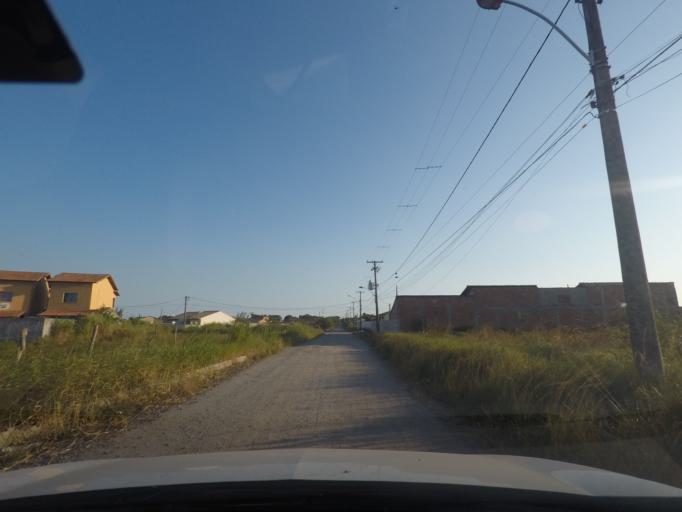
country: BR
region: Rio de Janeiro
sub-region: Marica
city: Marica
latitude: -22.9638
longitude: -42.9281
